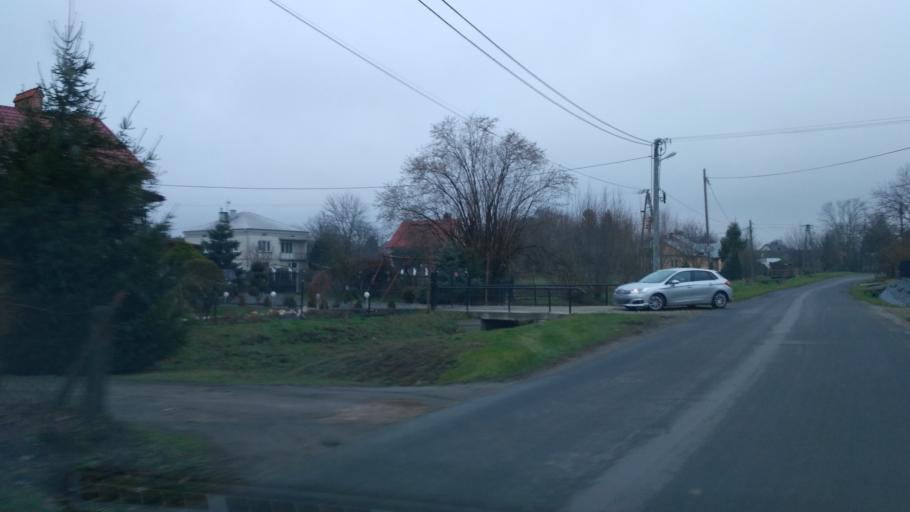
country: PL
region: Subcarpathian Voivodeship
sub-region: Powiat przeworski
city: Rozborz
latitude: 50.0614
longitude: 22.5415
